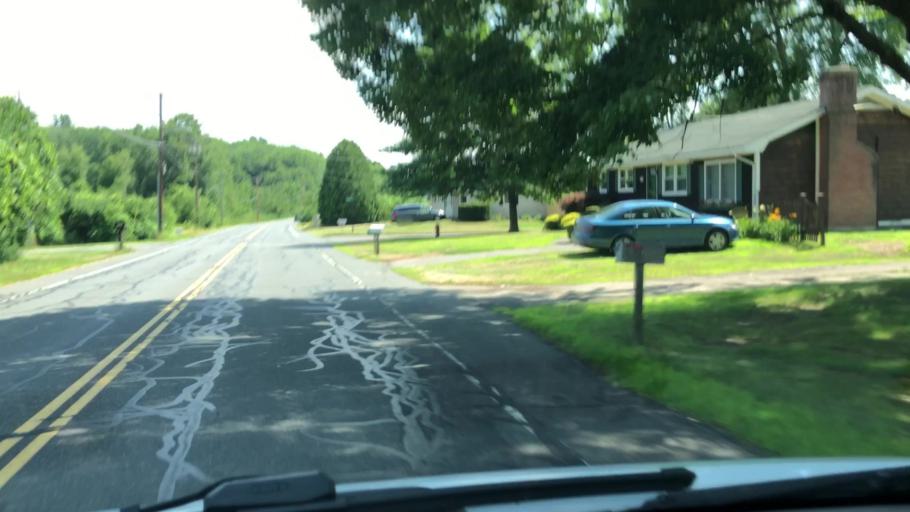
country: US
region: Massachusetts
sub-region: Hampshire County
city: Easthampton
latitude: 42.2985
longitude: -72.6732
